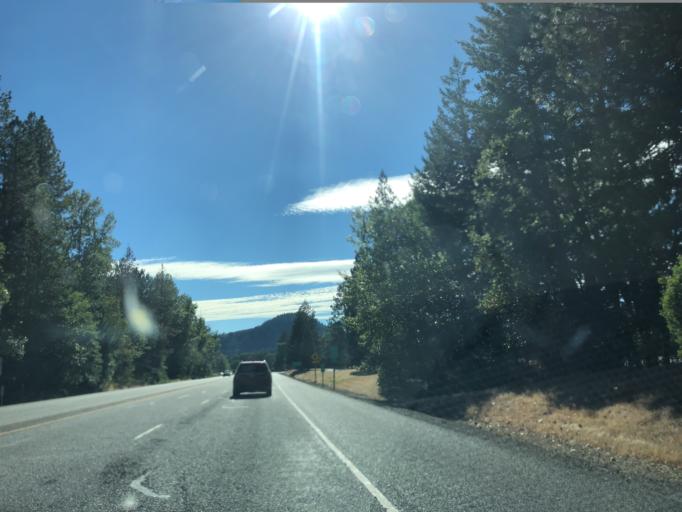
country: US
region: Oregon
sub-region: Josephine County
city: Redwood
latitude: 42.4112
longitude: -123.4225
